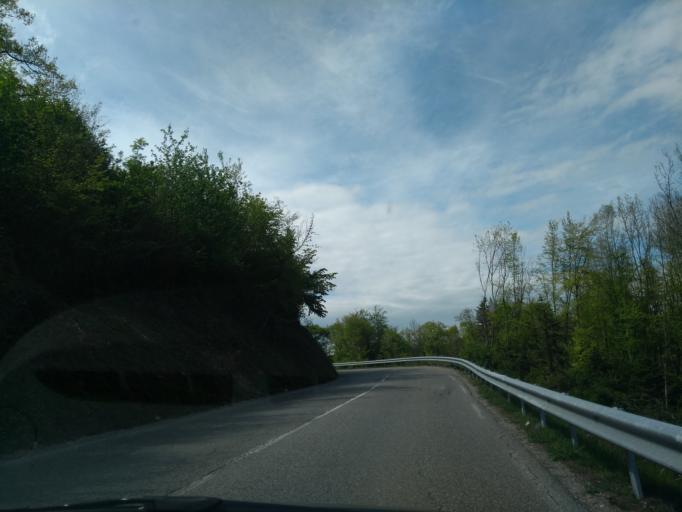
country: FR
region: Rhone-Alpes
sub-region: Departement de la Haute-Savoie
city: Chavanod
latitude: 45.8799
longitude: 6.0313
